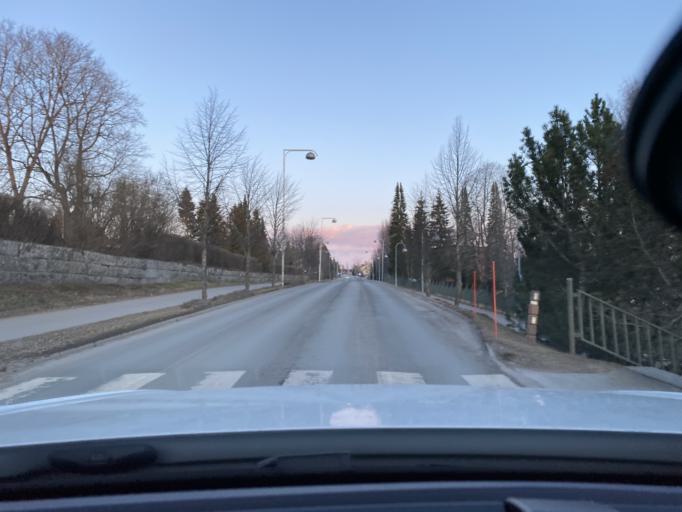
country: FI
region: Pirkanmaa
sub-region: Lounais-Pirkanmaa
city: Punkalaidun
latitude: 61.1144
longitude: 23.0960
